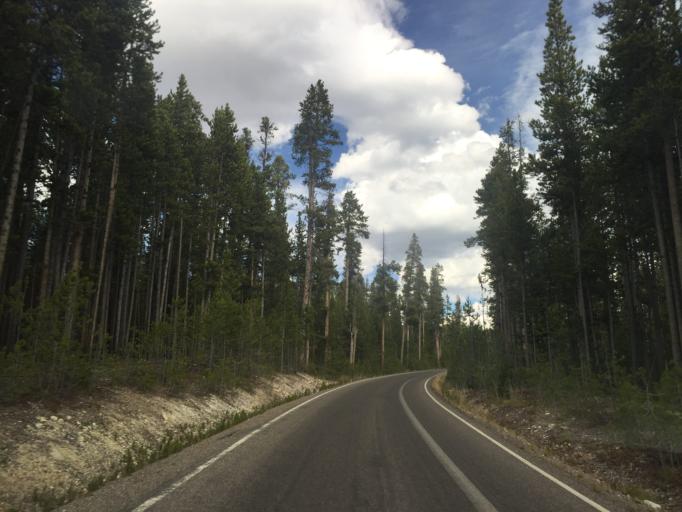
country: US
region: Montana
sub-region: Gallatin County
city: West Yellowstone
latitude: 44.7266
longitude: -110.4837
